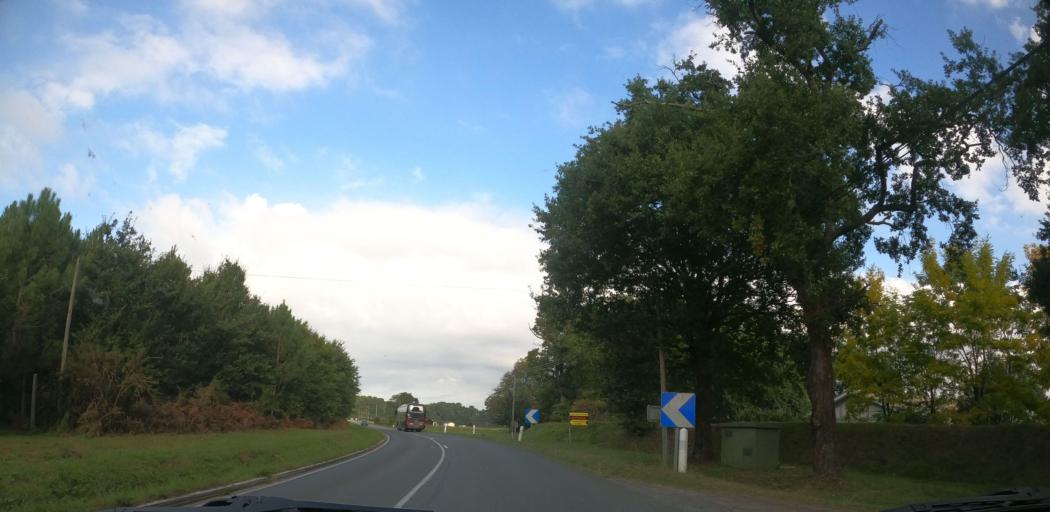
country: FR
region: Aquitaine
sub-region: Departement des Landes
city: Soustons
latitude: 43.7431
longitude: -1.3002
